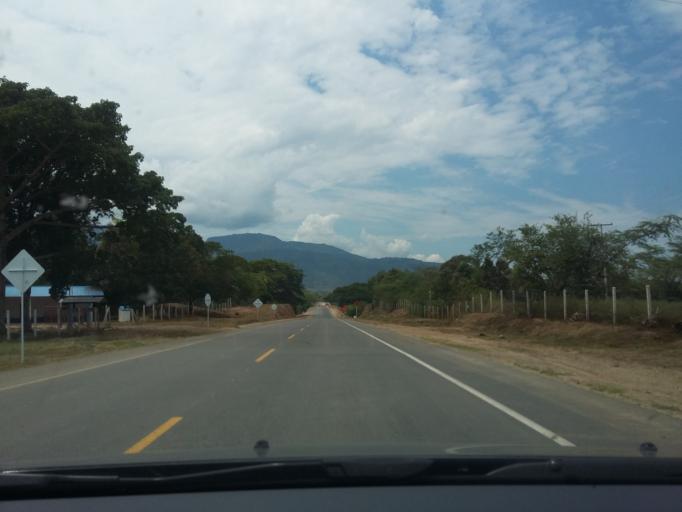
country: CO
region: Tolima
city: Ambalema
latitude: 4.8454
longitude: -74.7409
